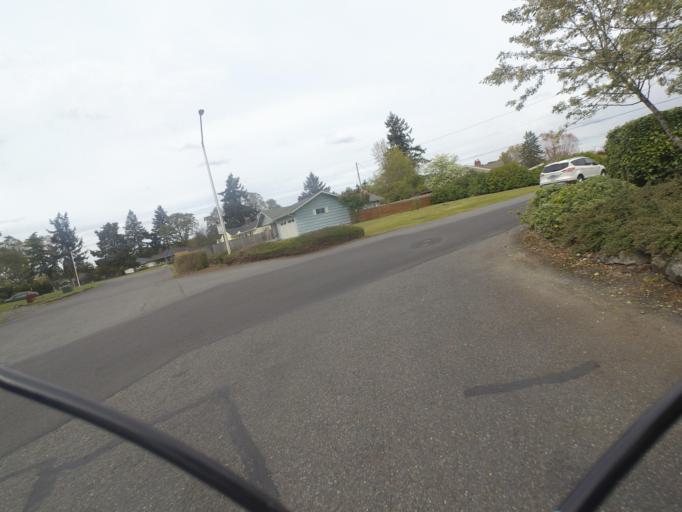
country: US
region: Washington
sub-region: Pierce County
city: McChord Air Force Base
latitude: 47.1604
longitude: -122.4890
